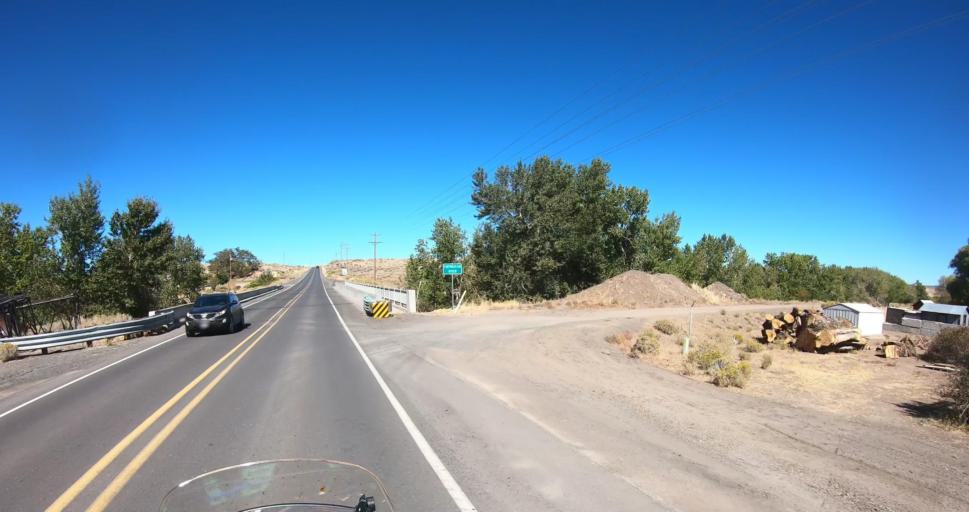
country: US
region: Oregon
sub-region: Lake County
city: Lakeview
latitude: 42.6952
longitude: -120.5458
